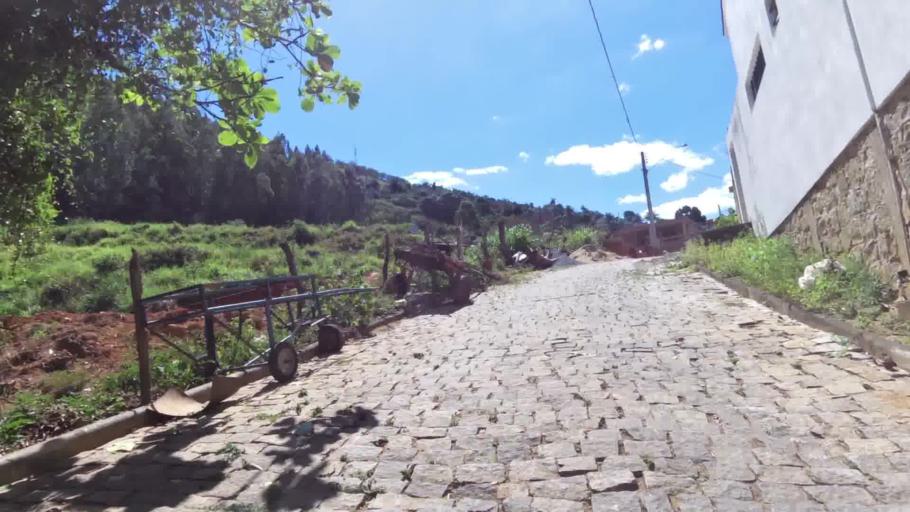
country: BR
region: Espirito Santo
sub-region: Rio Novo Do Sul
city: Rio Novo do Sul
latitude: -20.8637
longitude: -40.9392
